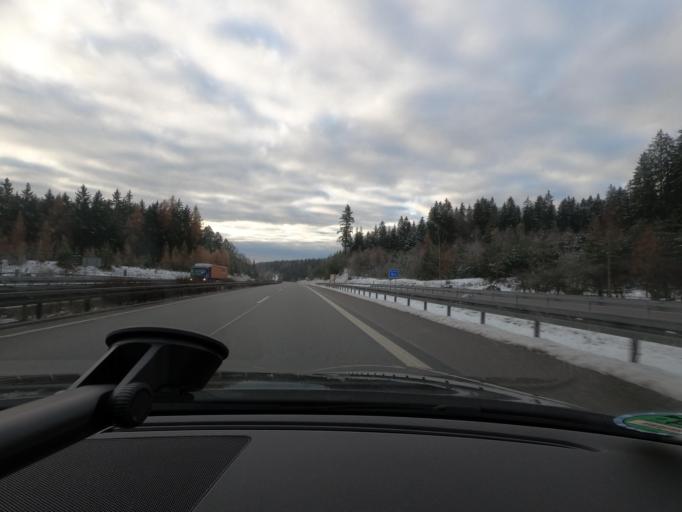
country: DE
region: Thuringia
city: Sankt Kilian
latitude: 50.5588
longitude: 10.7303
